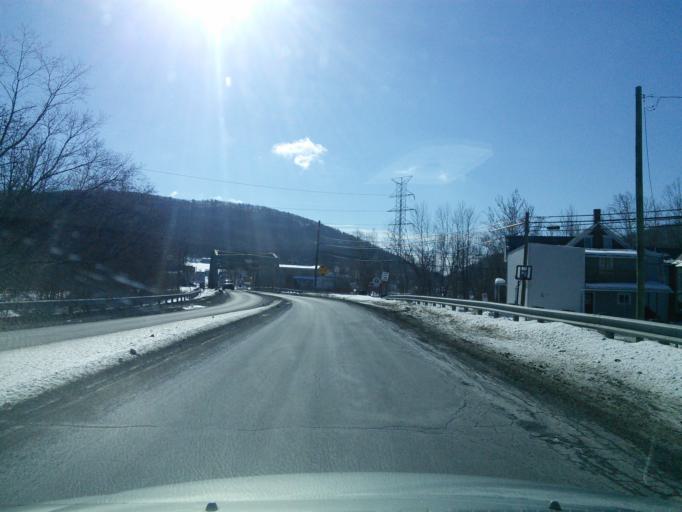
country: US
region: Pennsylvania
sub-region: Centre County
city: Milesburg
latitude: 40.9441
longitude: -77.7876
